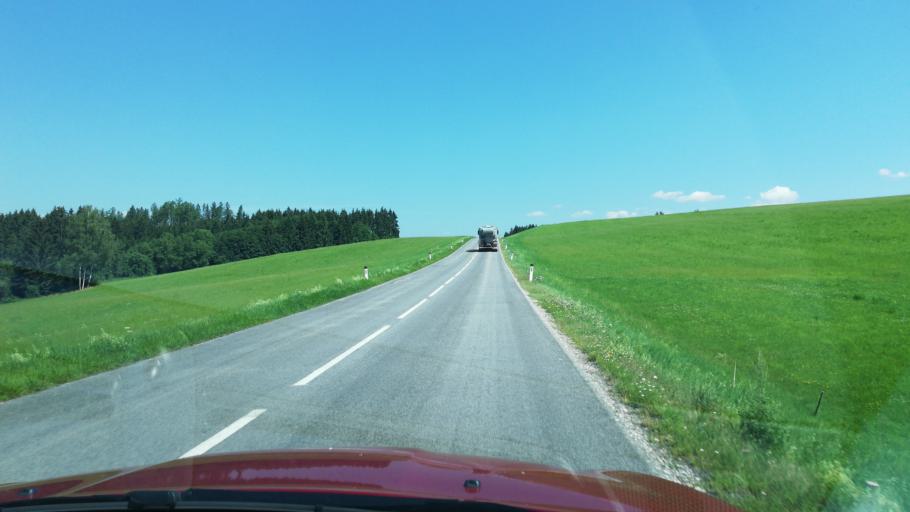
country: AT
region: Upper Austria
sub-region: Politischer Bezirk Urfahr-Umgebung
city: Herzogsdorf
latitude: 48.4658
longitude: 14.0587
